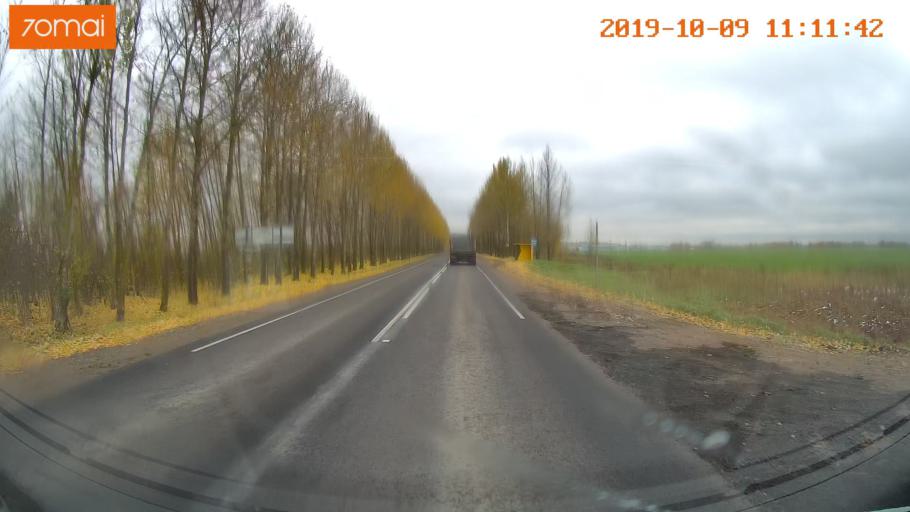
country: RU
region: Vologda
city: Vologda
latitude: 59.1706
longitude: 39.8230
